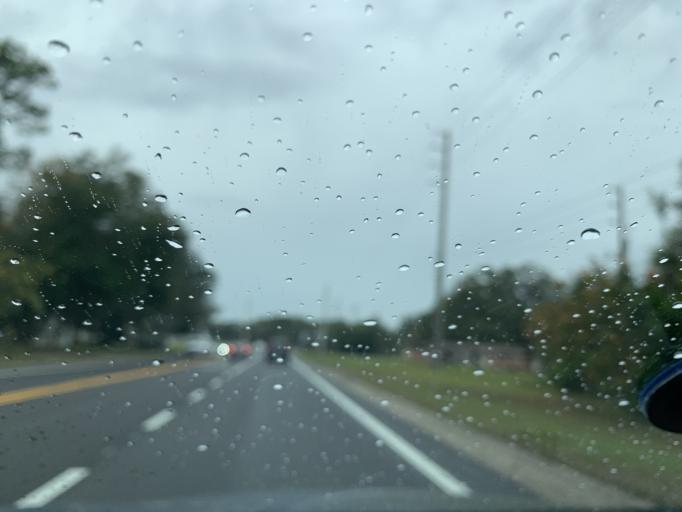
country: US
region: Florida
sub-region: Pasco County
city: Zephyrhills
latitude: 28.2519
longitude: -82.1955
